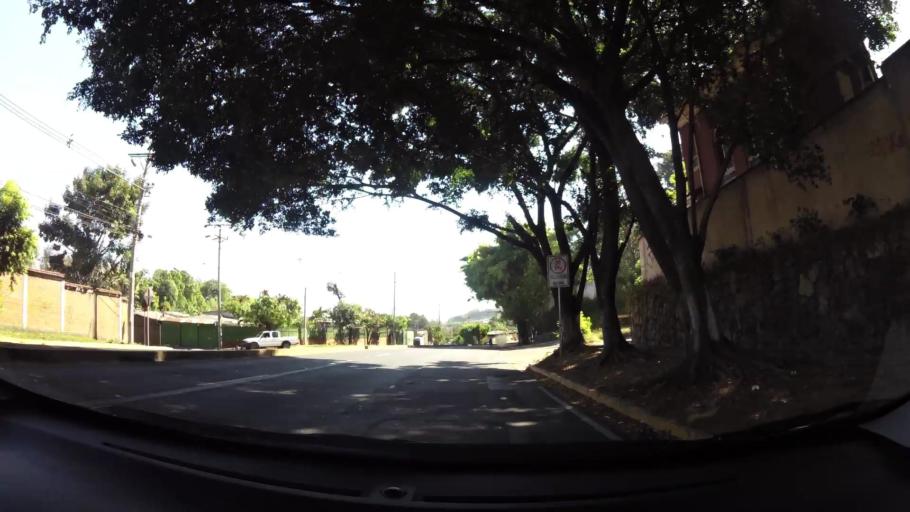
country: SV
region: La Libertad
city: Santa Tecla
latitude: 13.6664
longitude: -89.2840
